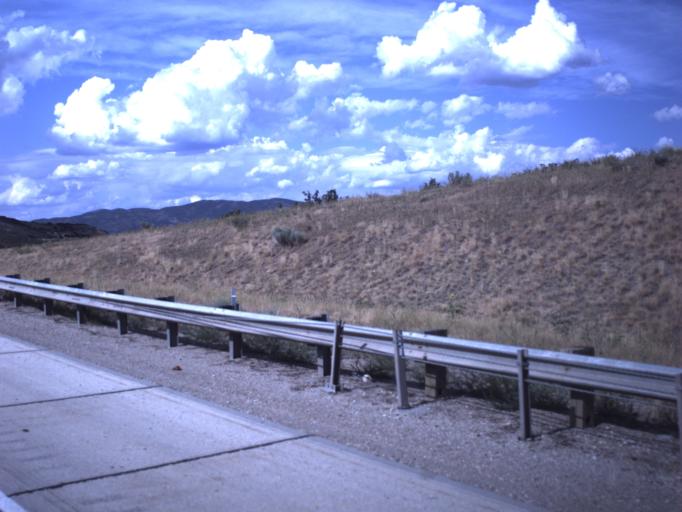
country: US
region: Utah
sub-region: Wasatch County
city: Heber
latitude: 40.5823
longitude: -111.4362
